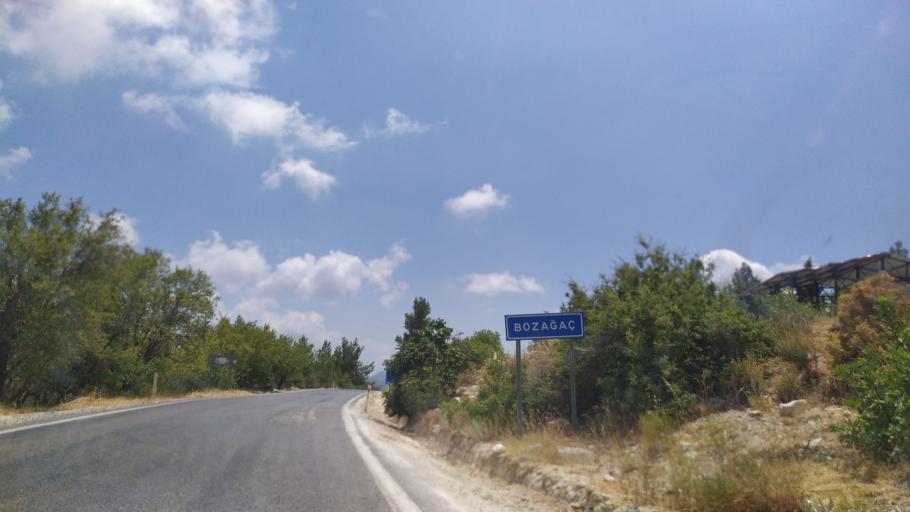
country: TR
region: Mersin
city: Gulnar
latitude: 36.2893
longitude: 33.3815
